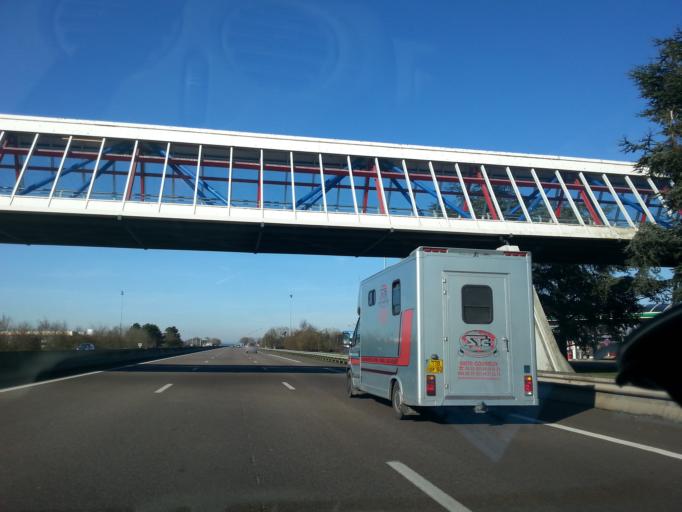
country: FR
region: Haute-Normandie
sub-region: Departement de l'Eure
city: Saint-Pierre-du-Vauvray
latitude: 49.2105
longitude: 1.2198
